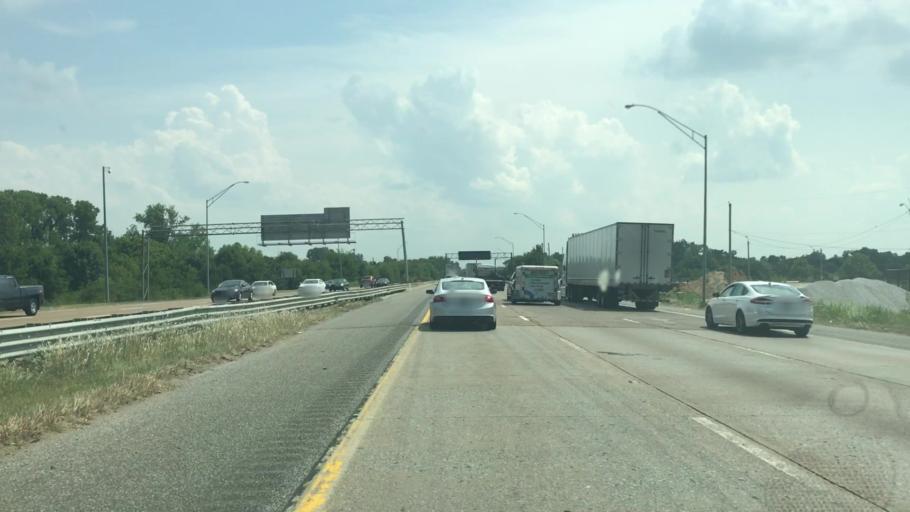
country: US
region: Tennessee
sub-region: Shelby County
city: Memphis
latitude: 35.1834
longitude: -90.0179
